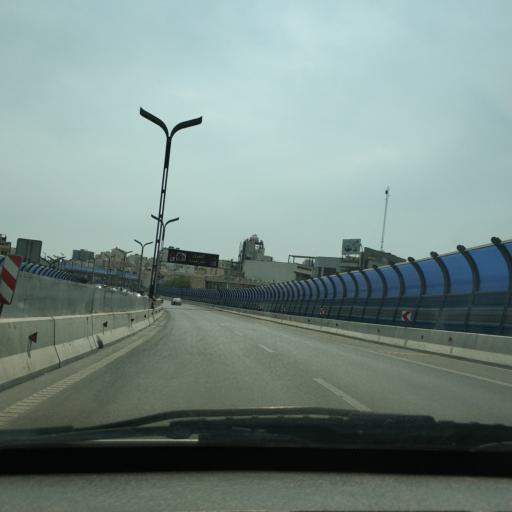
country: IR
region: Tehran
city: Tajrish
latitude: 35.7931
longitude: 51.4596
